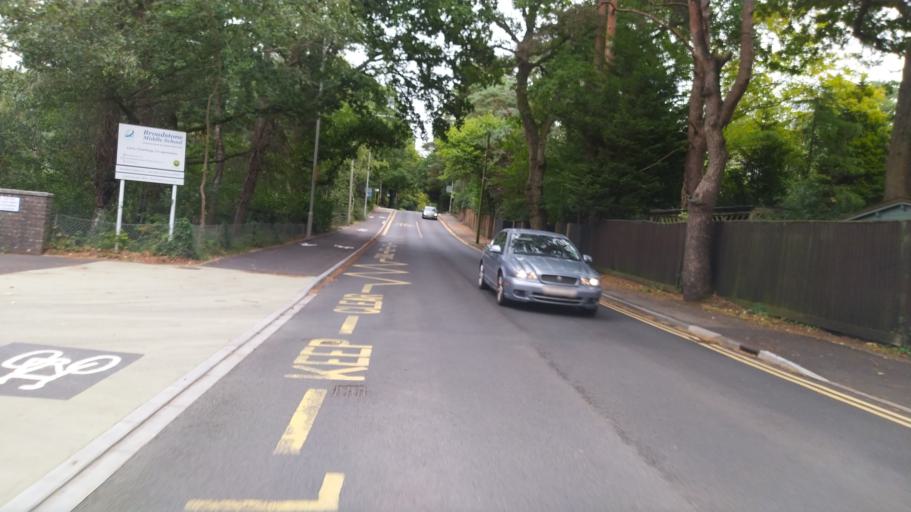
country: GB
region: England
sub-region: Dorset
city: Broadstone
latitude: 50.7636
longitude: -1.9855
